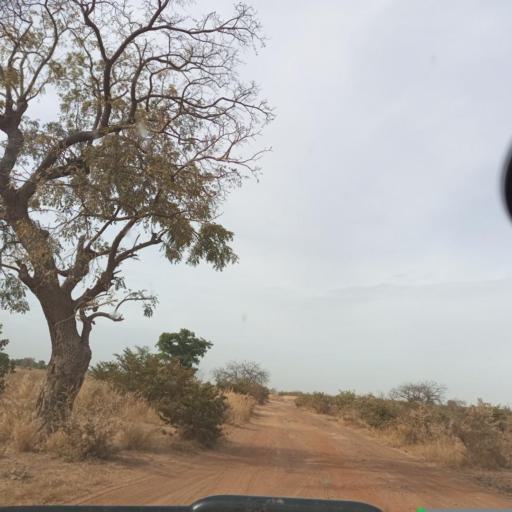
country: ML
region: Koulikoro
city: Koulikoro
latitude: 13.1077
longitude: -7.6233
